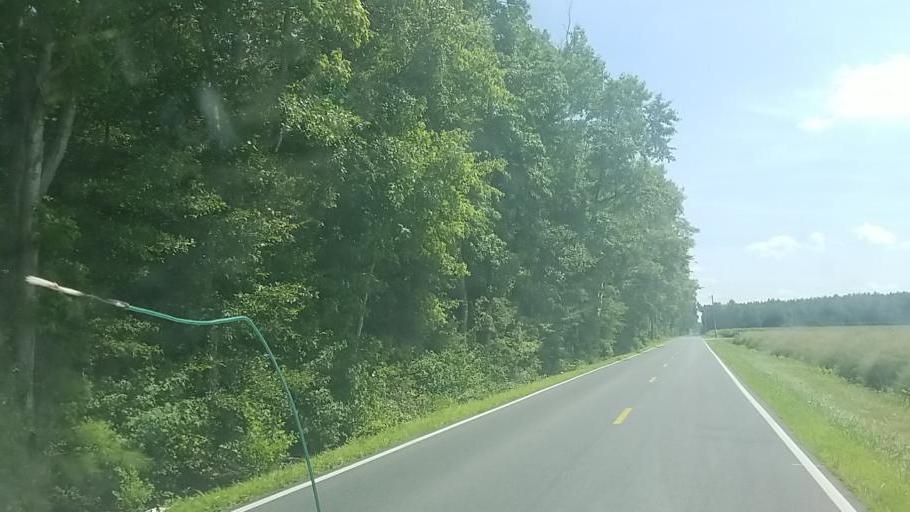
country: US
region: Maryland
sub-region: Wicomico County
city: Hebron
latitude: 38.4401
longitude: -75.6982
